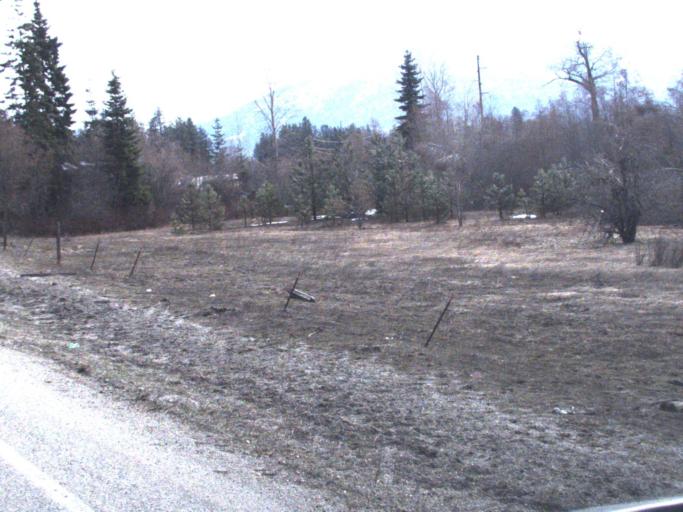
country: US
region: Washington
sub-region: Pend Oreille County
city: Newport
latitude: 48.4683
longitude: -117.3211
